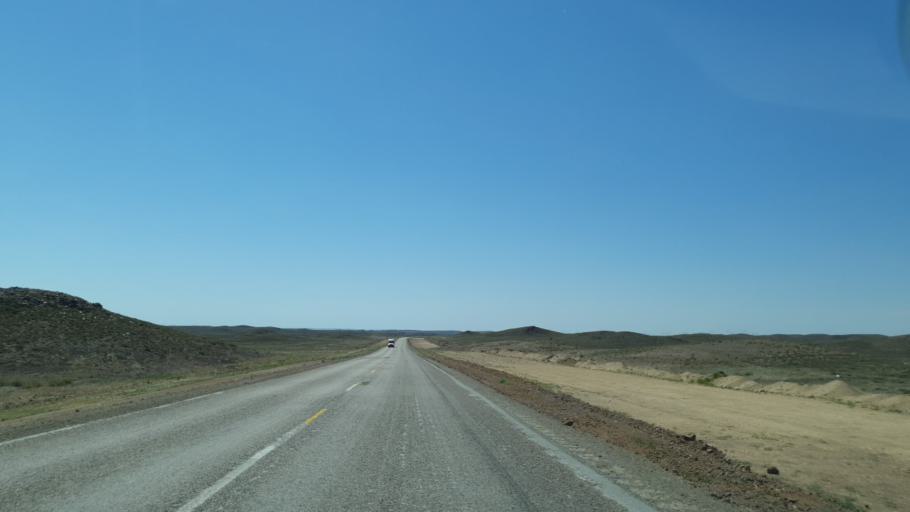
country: KZ
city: Priozersk
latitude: 45.7423
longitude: 73.4038
